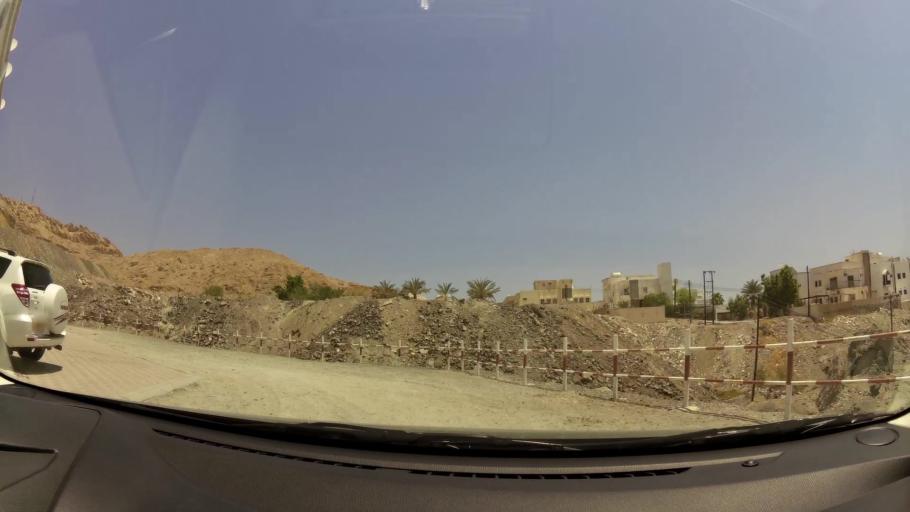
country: OM
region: Muhafazat Masqat
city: Muscat
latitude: 23.6101
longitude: 58.5363
